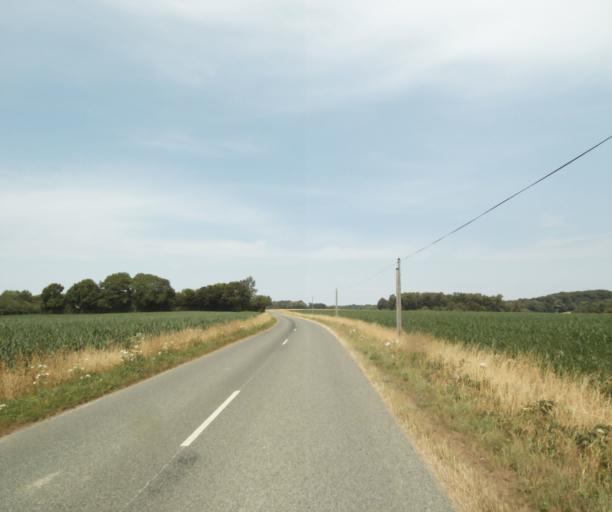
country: FR
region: Centre
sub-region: Departement d'Eure-et-Loir
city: Authon-du-Perche
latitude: 48.1810
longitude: 0.9446
